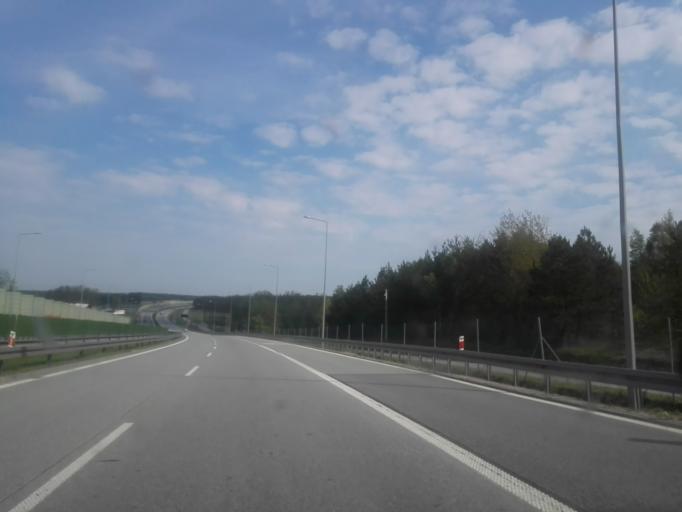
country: PL
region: Lodz Voivodeship
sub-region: Powiat rawski
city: Rawa Mazowiecka
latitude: 51.7053
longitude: 20.2204
